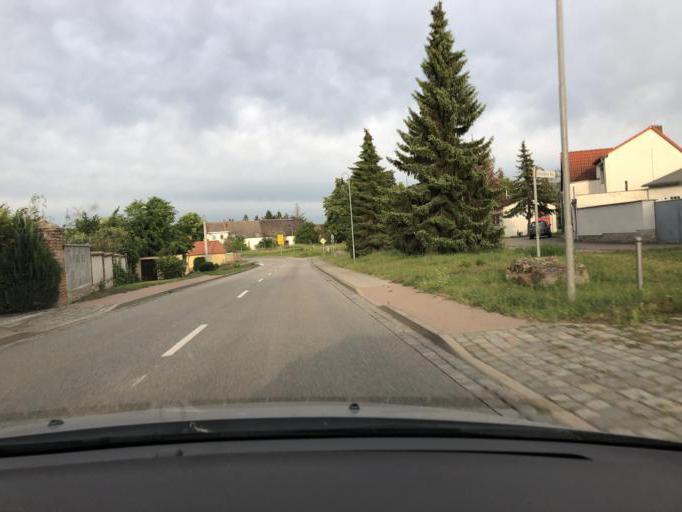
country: DE
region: Saxony-Anhalt
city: Grosskorbetha
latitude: 51.2239
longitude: 12.0291
